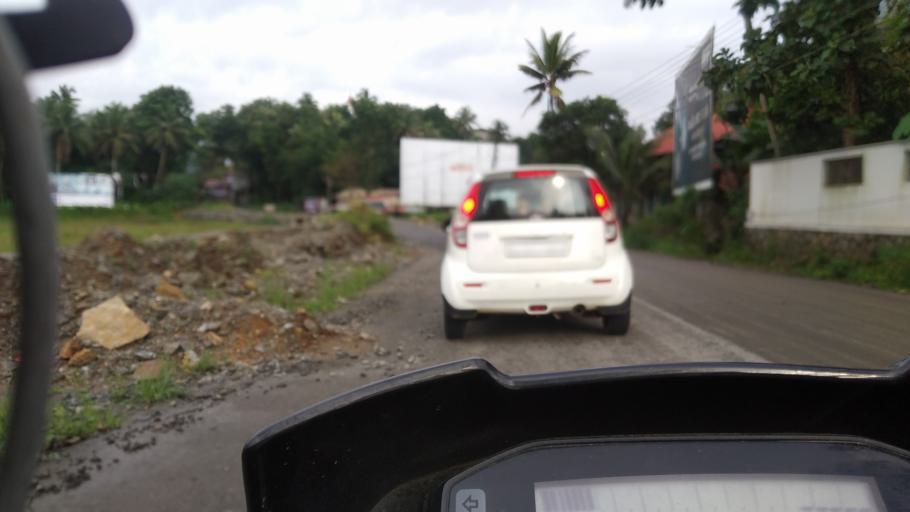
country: IN
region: Kerala
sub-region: Idukki
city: Kuttampuzha
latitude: 10.0504
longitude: 76.7313
